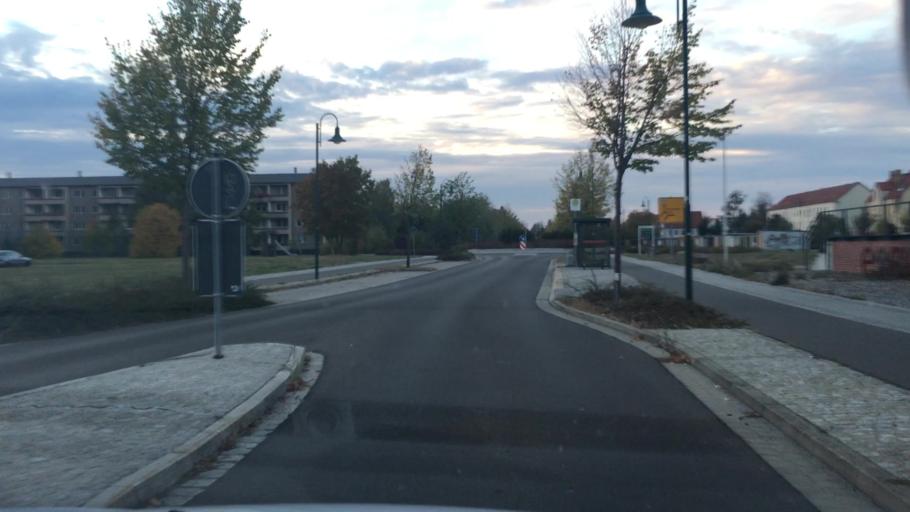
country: DE
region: Brandenburg
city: Welzow
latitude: 51.5799
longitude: 14.1692
